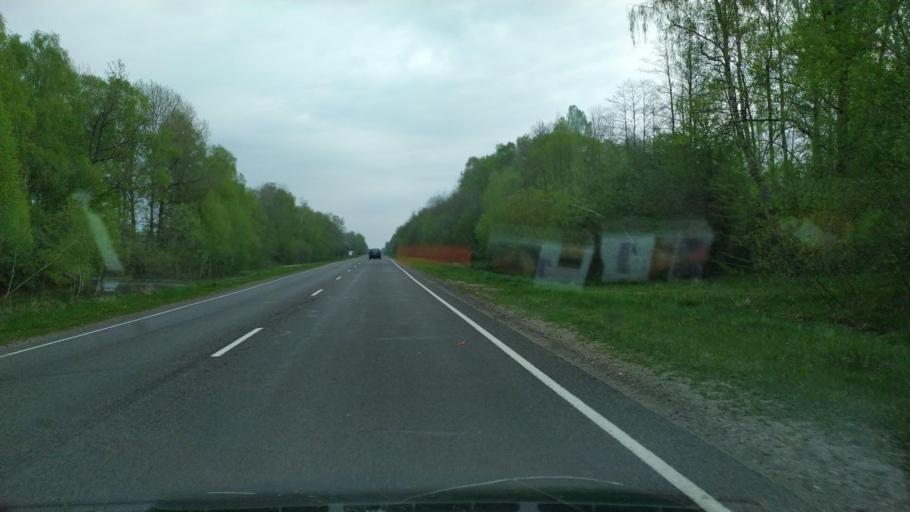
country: BY
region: Brest
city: Horad Kobryn
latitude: 52.3084
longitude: 24.5354
